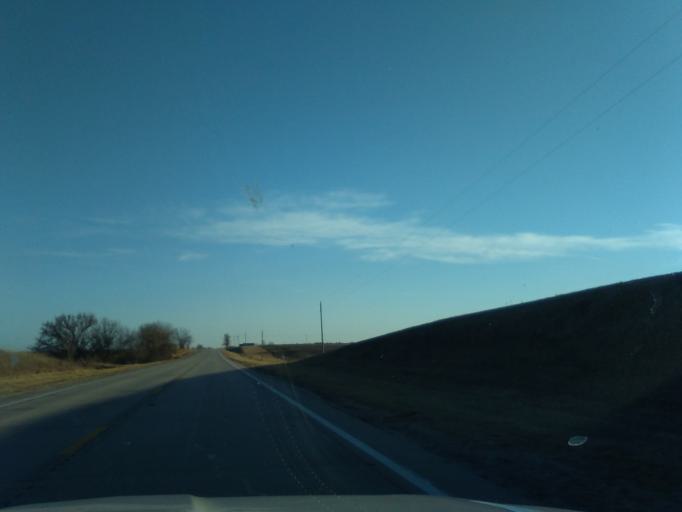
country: US
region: Nebraska
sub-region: Johnson County
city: Tecumseh
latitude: 40.4845
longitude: -96.1799
